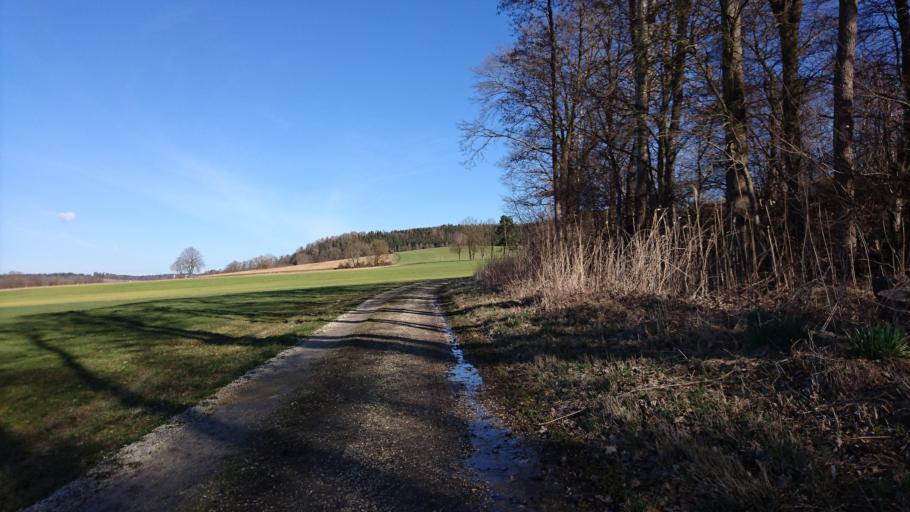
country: DE
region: Bavaria
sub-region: Swabia
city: Altenmunster
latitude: 48.4458
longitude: 10.6011
